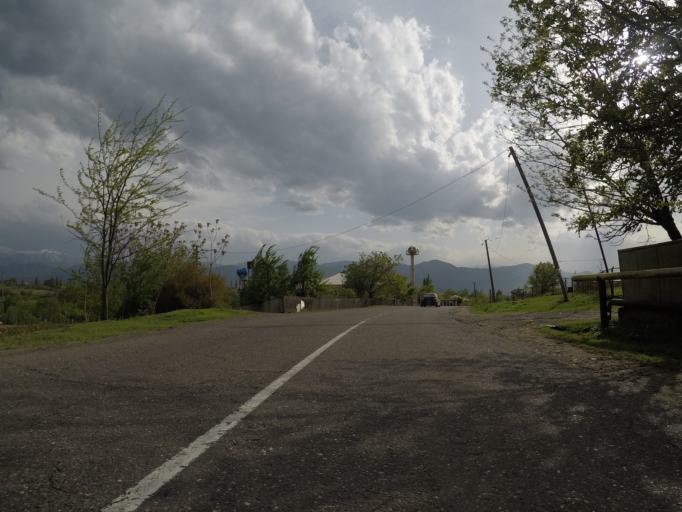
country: GE
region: Imereti
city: Zestap'oni
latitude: 42.1287
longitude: 43.0674
